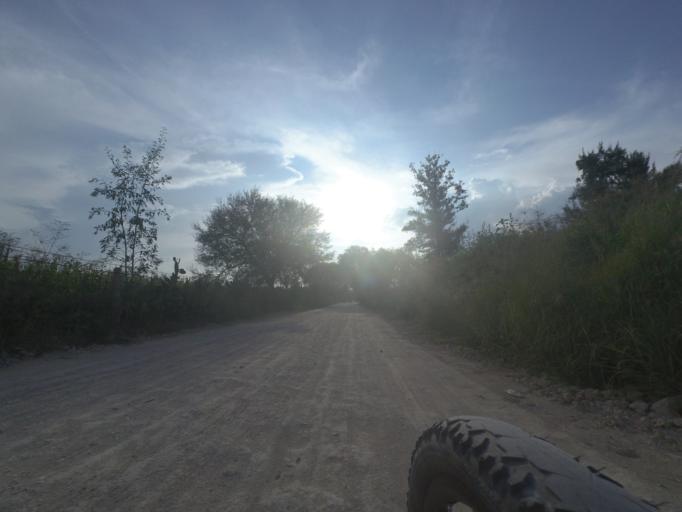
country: MX
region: Aguascalientes
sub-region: Aguascalientes
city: La Loma de los Negritos
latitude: 21.7752
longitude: -102.3628
